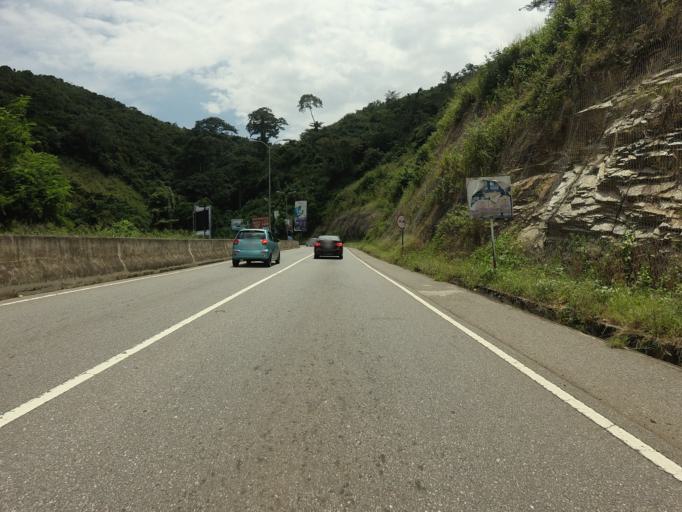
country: GH
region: Eastern
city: Aburi
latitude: 5.7891
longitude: -0.1885
